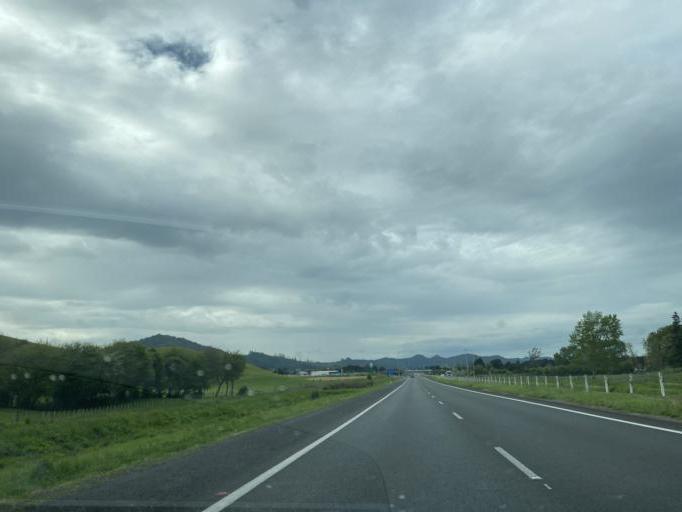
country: NZ
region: Waikato
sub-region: Waikato District
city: Ngaruawahia
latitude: -37.6304
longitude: 175.2063
